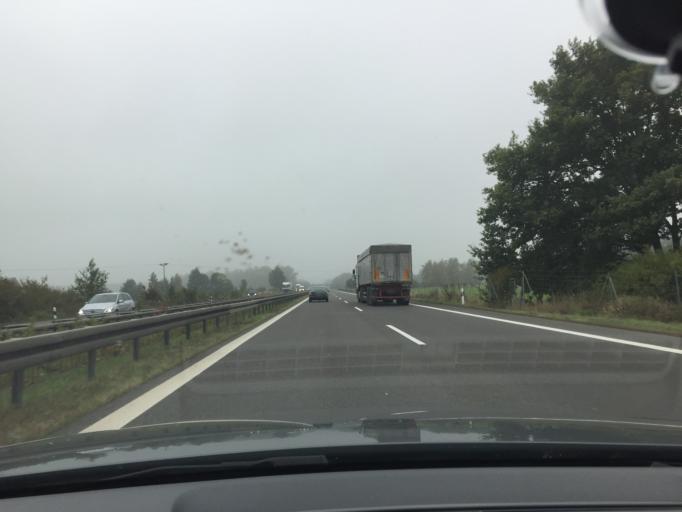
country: DE
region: Brandenburg
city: Calau
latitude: 51.7649
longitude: 13.8652
